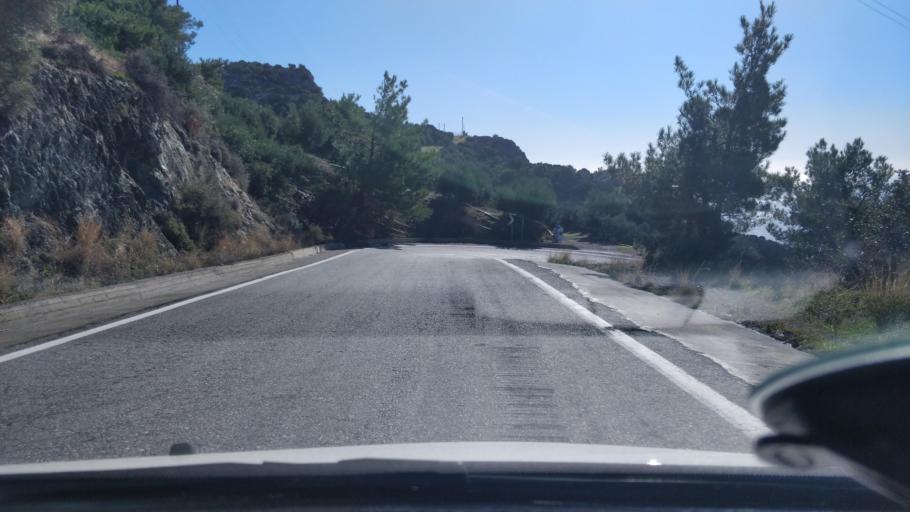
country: GR
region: Crete
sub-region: Nomos Irakleiou
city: Arkalochori
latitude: 35.0059
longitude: 25.4376
